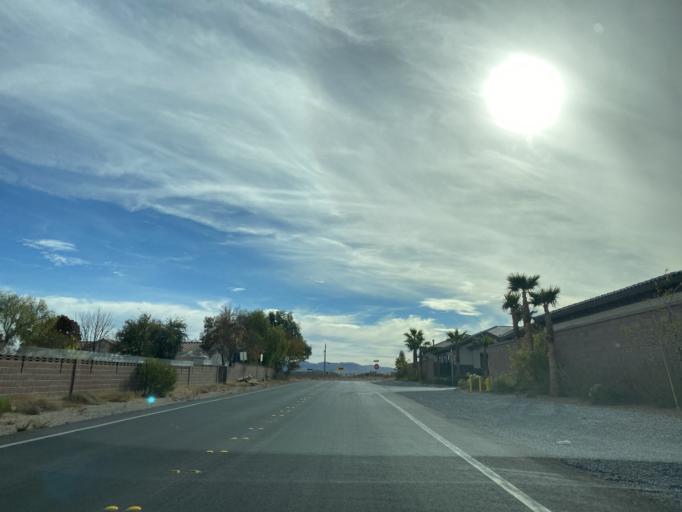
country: US
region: Nevada
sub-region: Clark County
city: Enterprise
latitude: 36.0347
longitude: -115.2676
